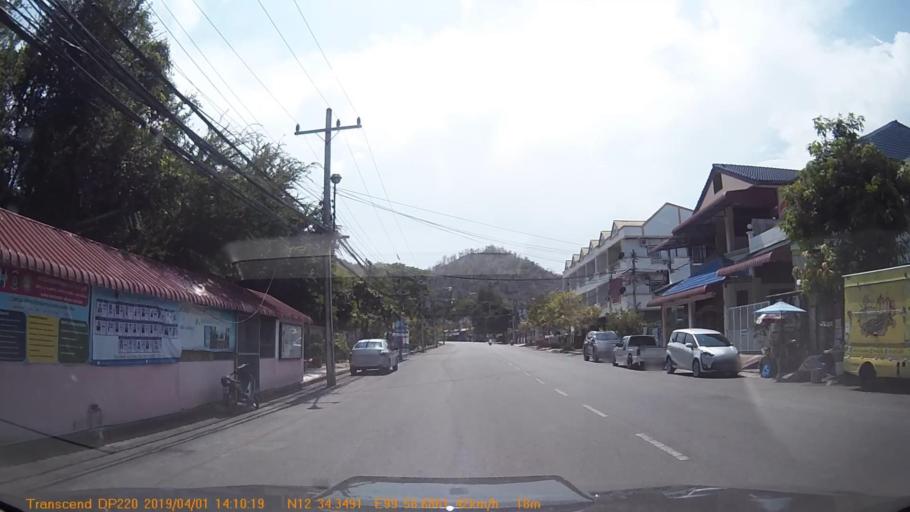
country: TH
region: Prachuap Khiri Khan
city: Hua Hin
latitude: 12.5724
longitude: 99.9444
